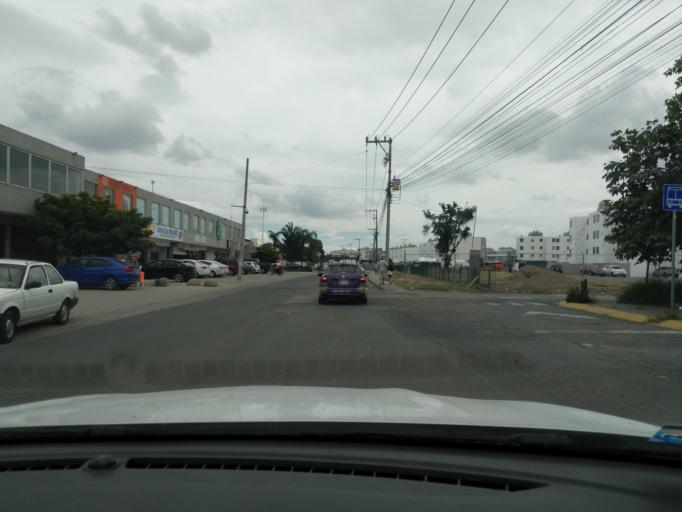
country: MX
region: Jalisco
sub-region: Zapopan
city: La Cuchilla (Extramuros de Tesistan)
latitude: 20.7843
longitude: -103.4767
